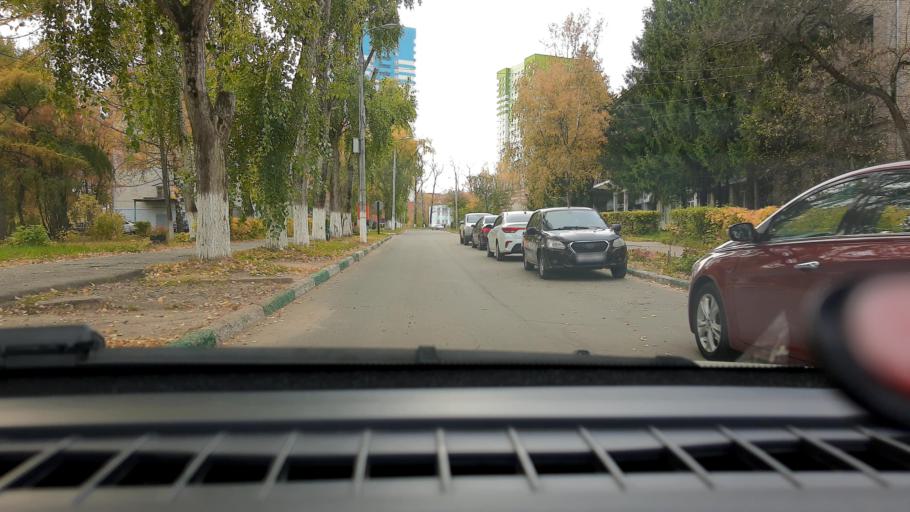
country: RU
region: Nizjnij Novgorod
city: Nizhniy Novgorod
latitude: 56.2427
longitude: 43.9578
